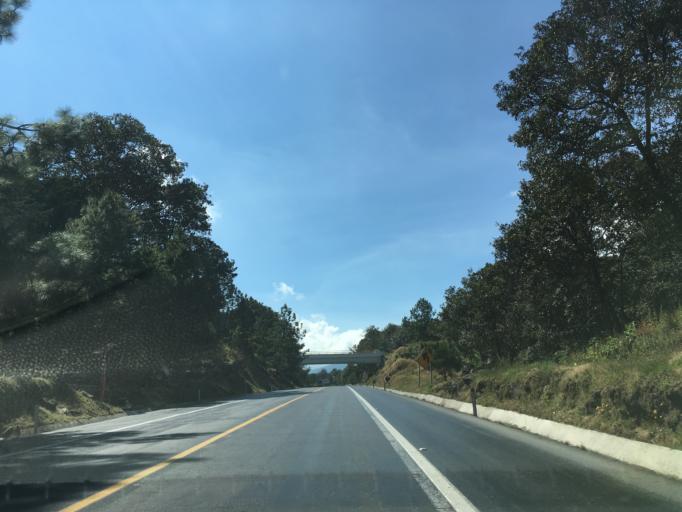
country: MX
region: Michoacan
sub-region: Patzcuaro
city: Santa Maria Huiramangaro (San Juan Tumbio)
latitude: 19.4876
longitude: -101.7190
